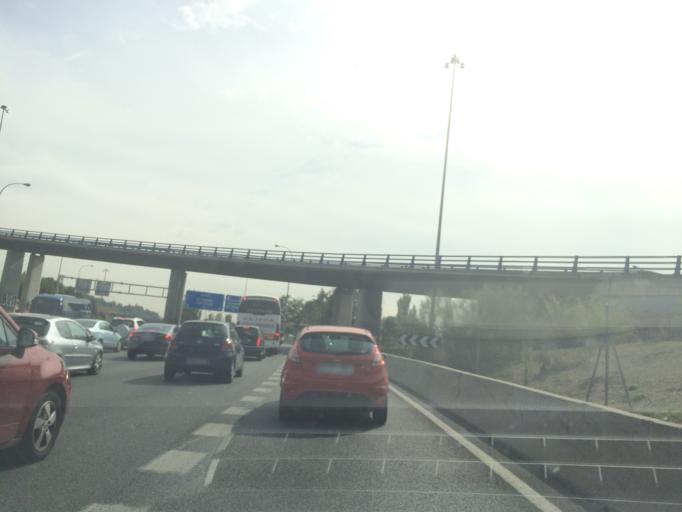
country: ES
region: Madrid
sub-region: Provincia de Madrid
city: Moncloa-Aravaca
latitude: 40.4531
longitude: -3.7436
